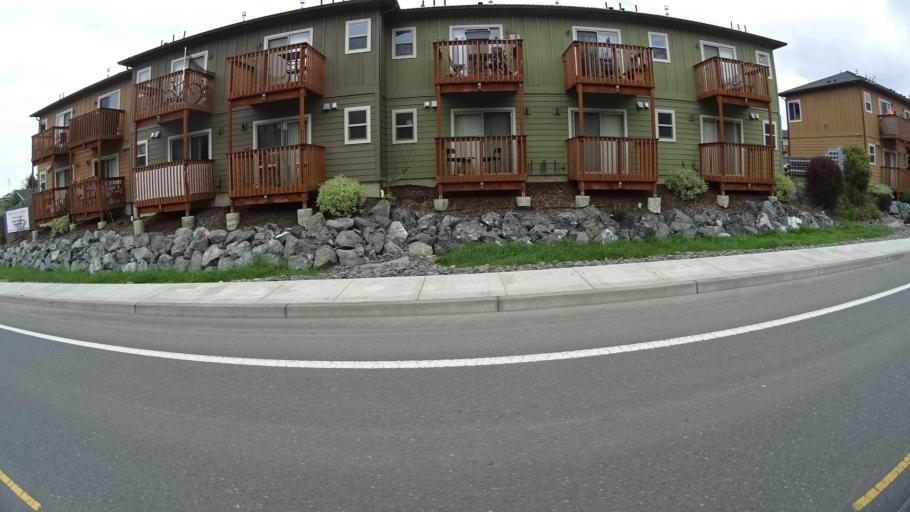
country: US
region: California
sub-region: Humboldt County
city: Arcata
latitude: 40.8794
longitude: -124.0888
